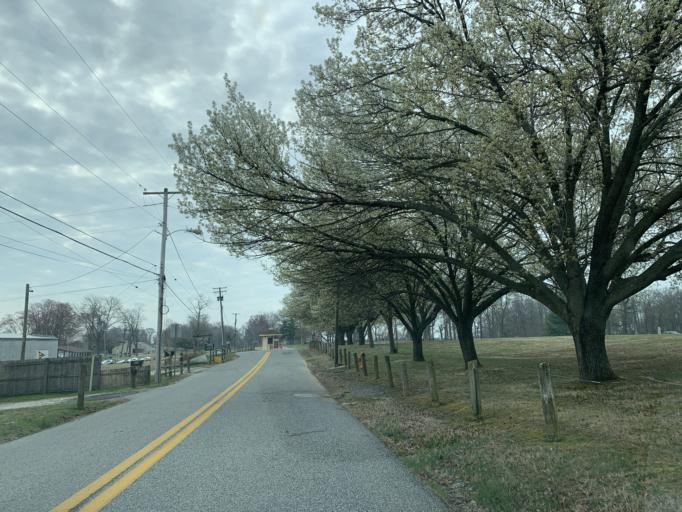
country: US
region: Maryland
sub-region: Baltimore County
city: Edgemere
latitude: 39.2541
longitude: -76.4062
